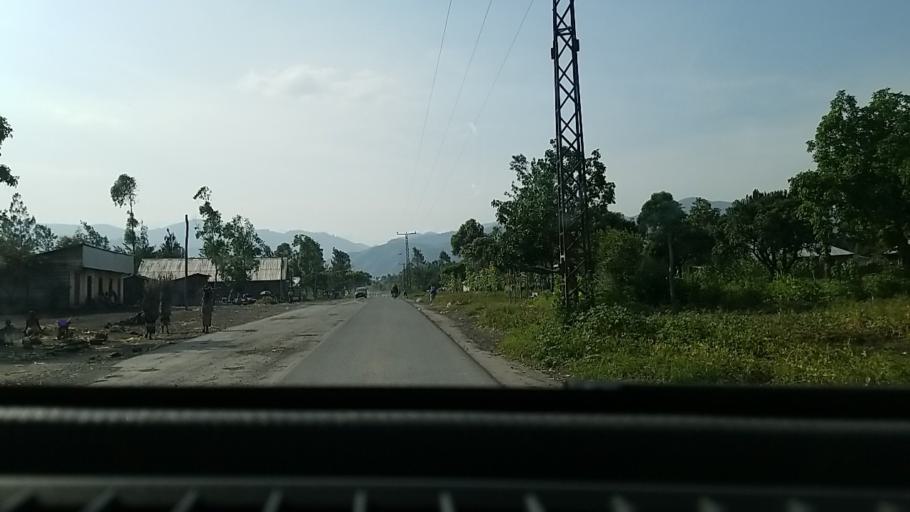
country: CD
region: Nord Kivu
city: Sake
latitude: -1.5769
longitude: 29.0731
